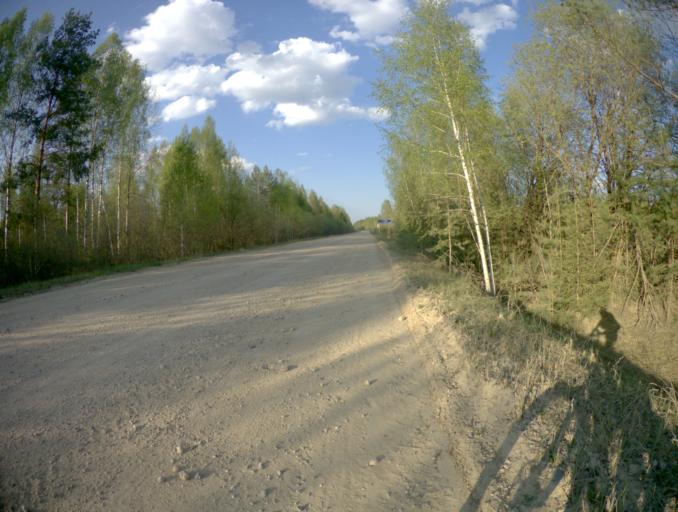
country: RU
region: Ivanovo
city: Yuzha
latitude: 56.5596
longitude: 41.8375
